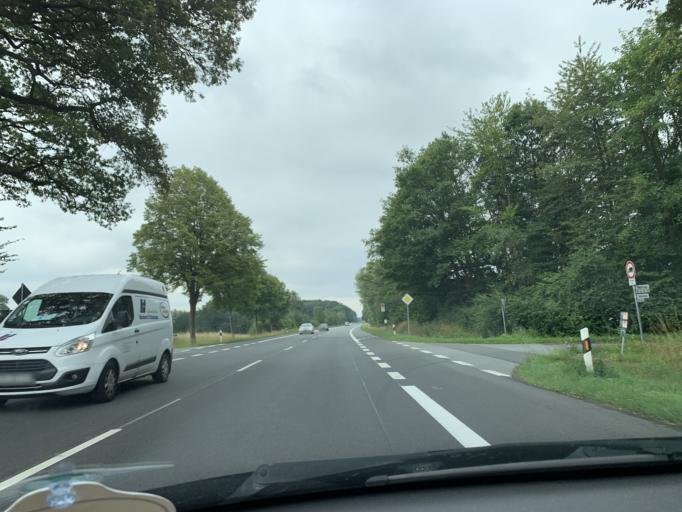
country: DE
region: North Rhine-Westphalia
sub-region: Regierungsbezirk Munster
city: Warendorf
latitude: 51.9224
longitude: 8.0349
